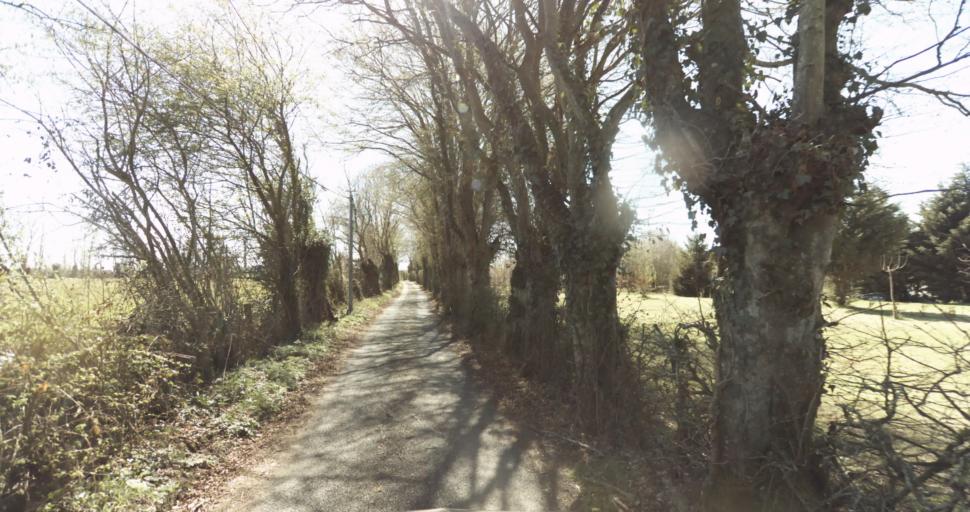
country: FR
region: Lower Normandy
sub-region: Departement du Calvados
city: Livarot
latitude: 49.0163
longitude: 0.1097
